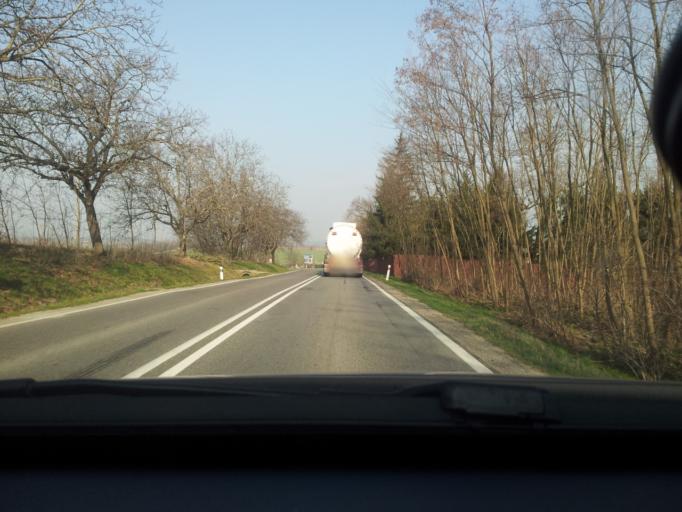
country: SK
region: Trnavsky
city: Hlohovec
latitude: 48.3569
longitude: 17.9367
